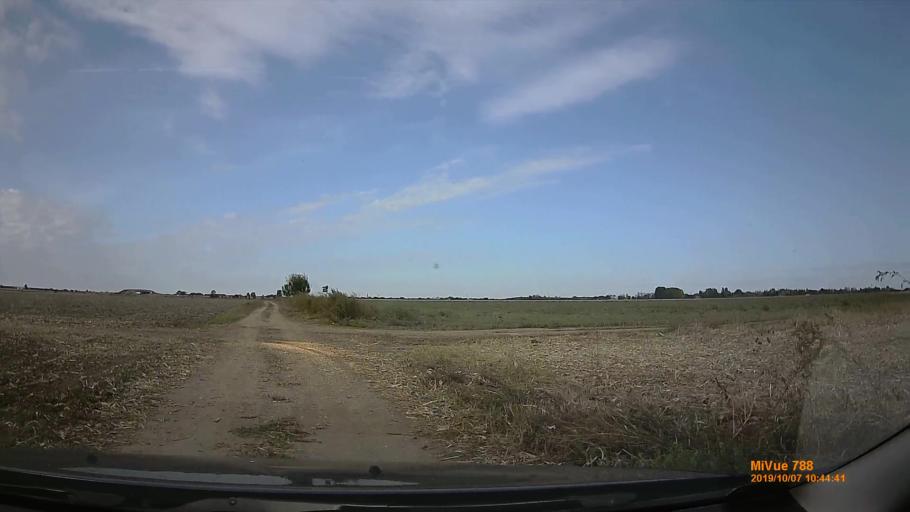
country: HU
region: Bekes
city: Kondoros
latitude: 46.7354
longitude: 20.8278
